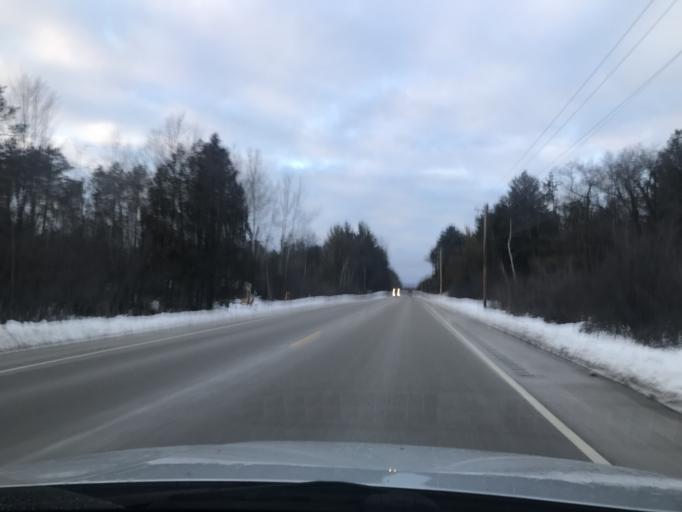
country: US
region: Wisconsin
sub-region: Marinette County
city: Marinette
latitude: 45.1287
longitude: -87.6863
